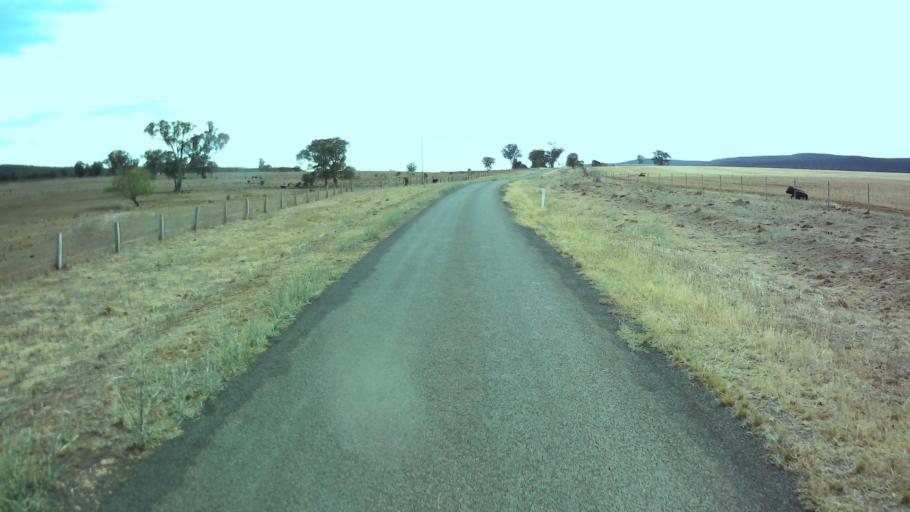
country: AU
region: New South Wales
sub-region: Weddin
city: Grenfell
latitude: -33.8357
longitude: 148.2695
